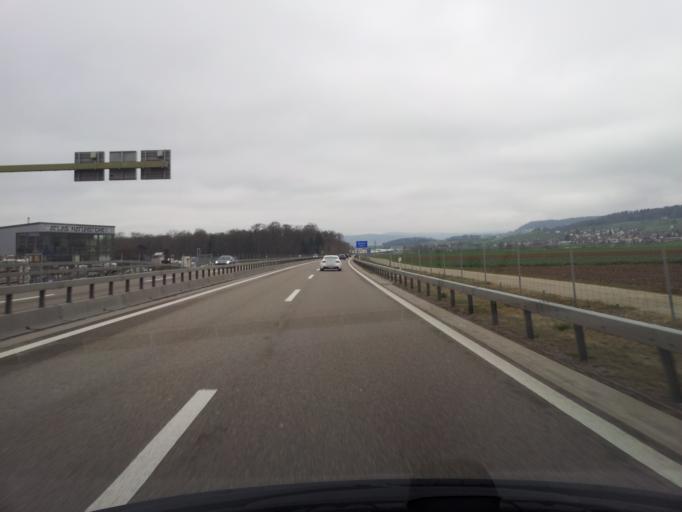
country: CH
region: Zurich
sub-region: Bezirk Andelfingen
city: Marthalen
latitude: 47.6359
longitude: 8.6619
